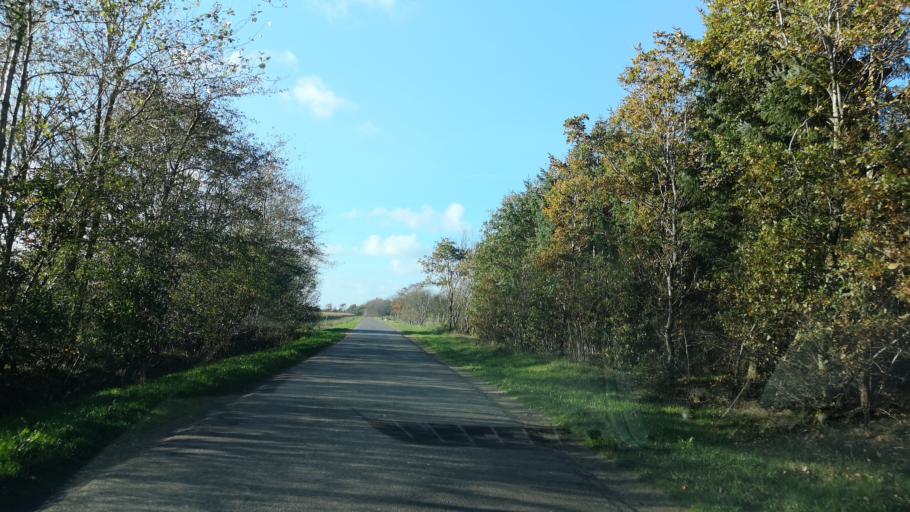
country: DK
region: Central Jutland
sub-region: Ringkobing-Skjern Kommune
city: Tarm
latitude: 55.8273
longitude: 8.3934
